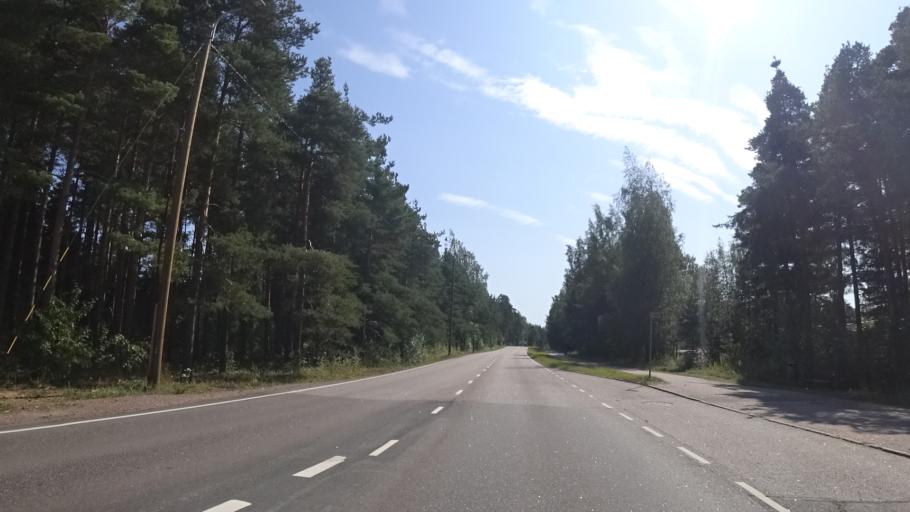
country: FI
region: Kymenlaakso
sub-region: Kotka-Hamina
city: Karhula
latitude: 60.5027
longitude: 26.9624
